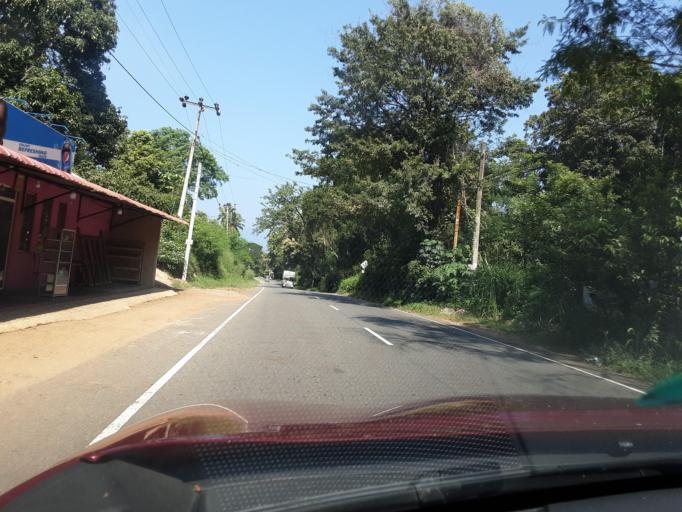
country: LK
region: Uva
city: Badulla
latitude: 7.1917
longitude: 81.0285
